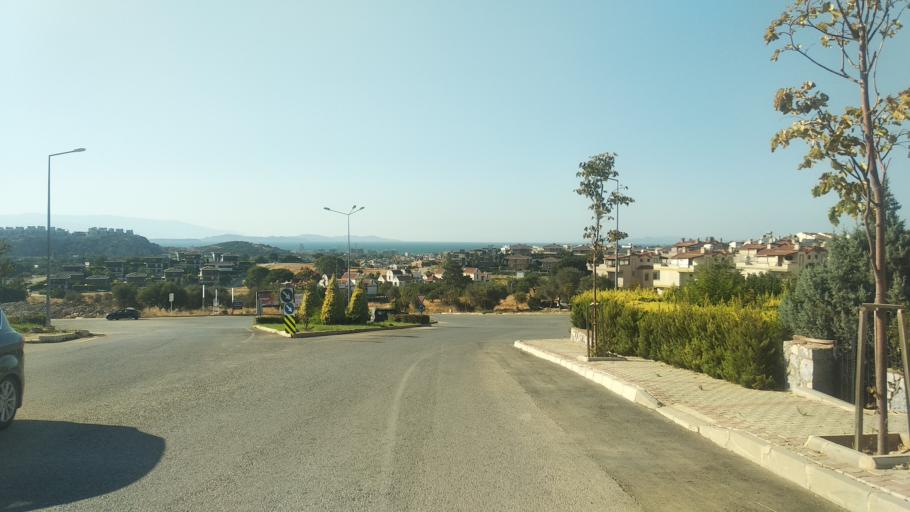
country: TR
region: Izmir
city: Urla
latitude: 38.3597
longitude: 26.8797
